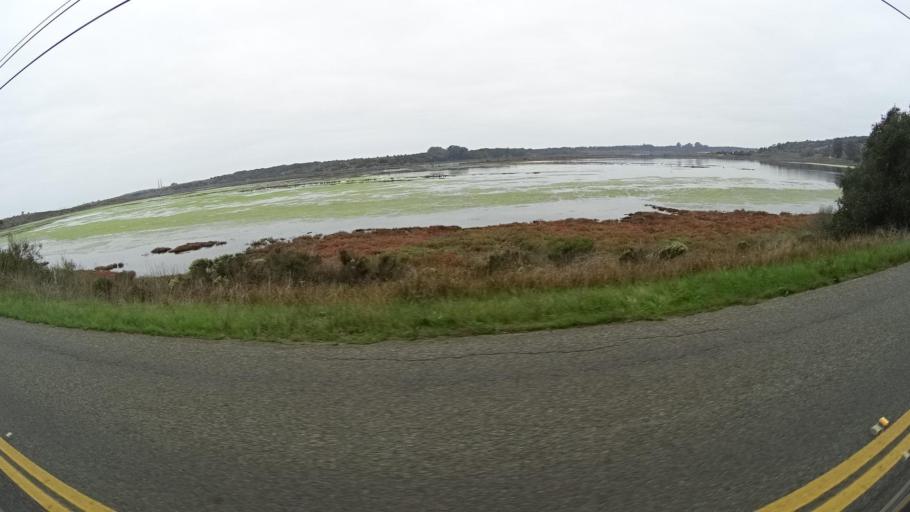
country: US
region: California
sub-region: Monterey County
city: Elkhorn
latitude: 36.8338
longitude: -121.7322
